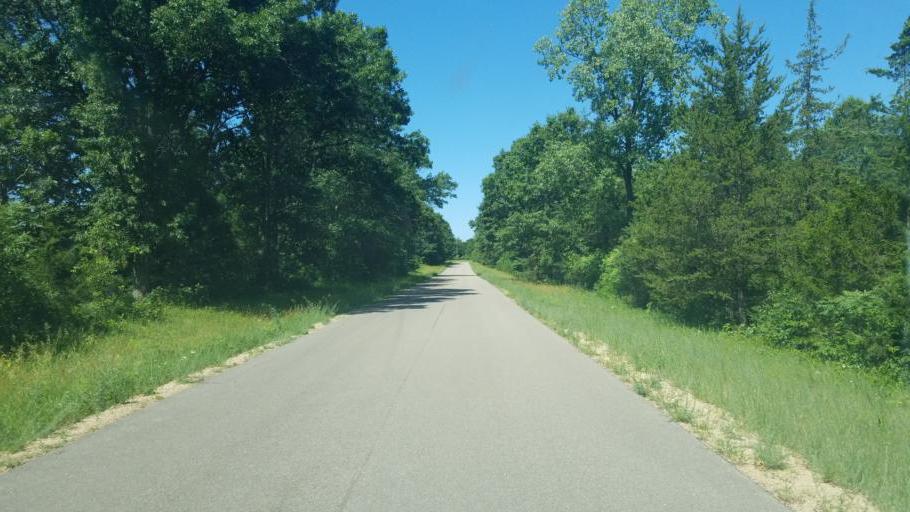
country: US
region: Wisconsin
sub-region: Adams County
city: Adams
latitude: 43.8694
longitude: -89.9416
